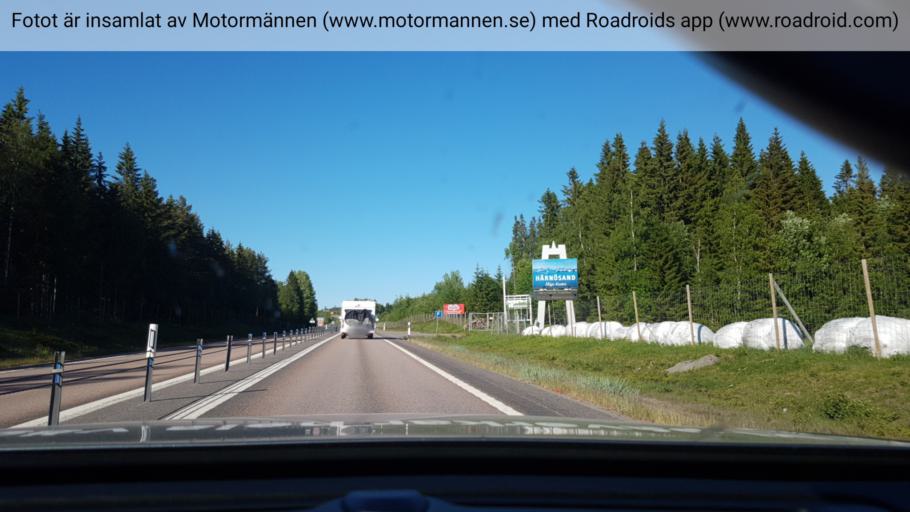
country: SE
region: Vaesternorrland
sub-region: Haernoesands Kommun
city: Haernoesand
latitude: 62.5927
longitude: 17.7971
